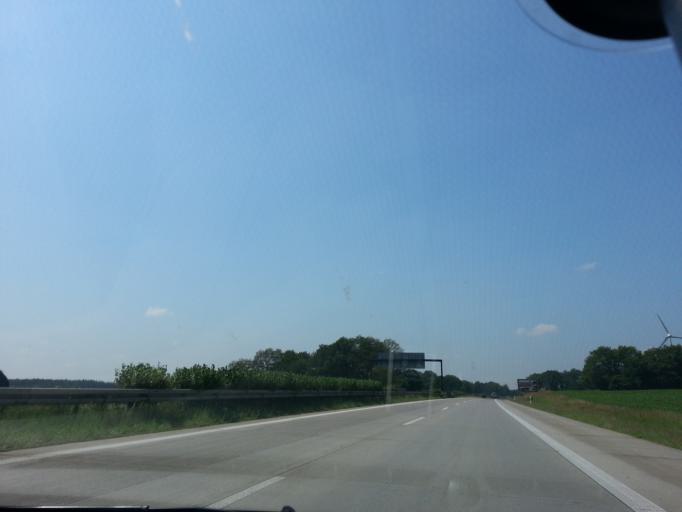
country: DE
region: Brandenburg
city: Wittstock
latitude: 53.1378
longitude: 12.4353
